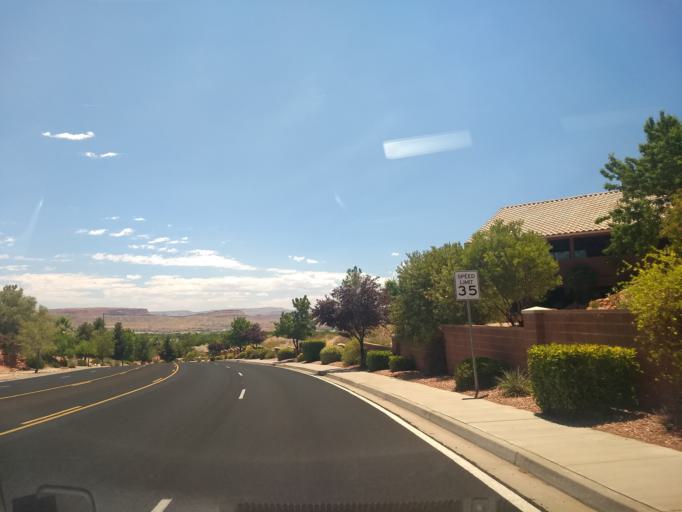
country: US
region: Utah
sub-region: Washington County
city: Washington
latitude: 37.1451
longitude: -113.5303
